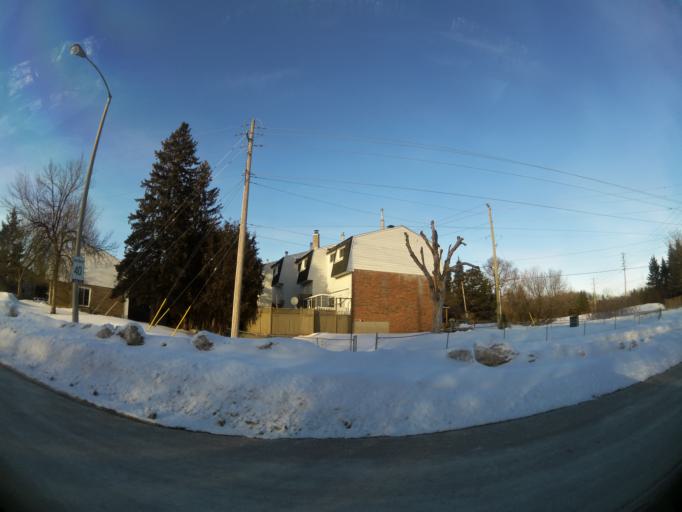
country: CA
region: Ontario
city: Ottawa
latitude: 45.4354
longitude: -75.5448
